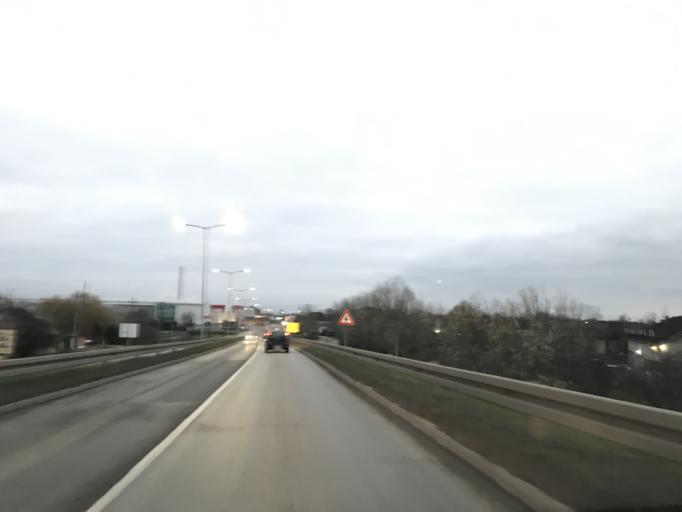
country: RS
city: Veternik
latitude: 45.2811
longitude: 19.7813
